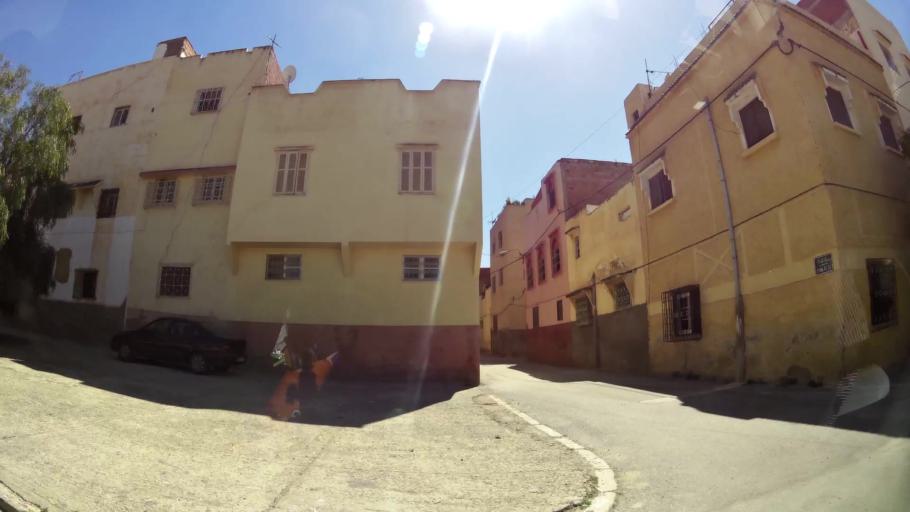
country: MA
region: Meknes-Tafilalet
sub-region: Meknes
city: Meknes
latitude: 33.8833
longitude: -5.5632
